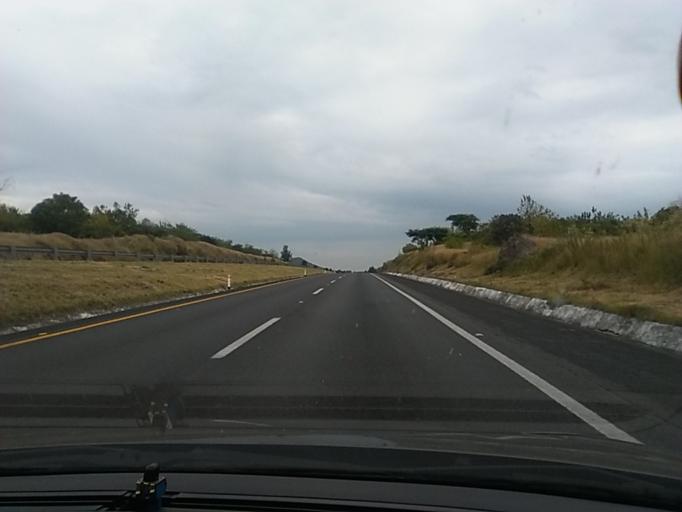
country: MX
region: Michoacan
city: Churintzio
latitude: 20.1129
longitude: -102.0438
